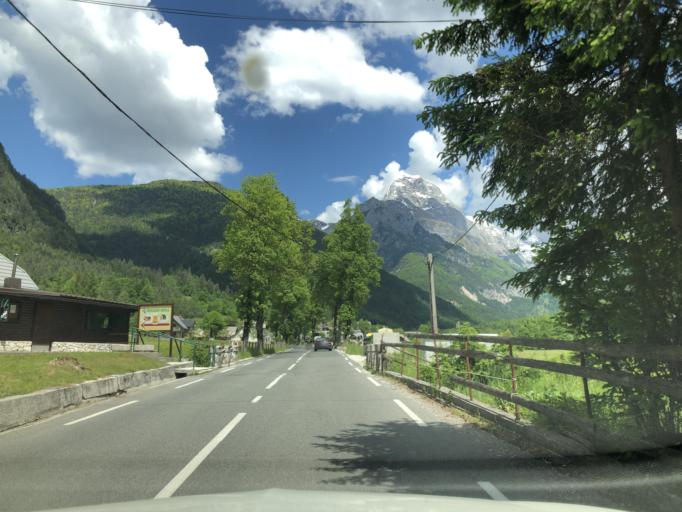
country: SI
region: Bovec
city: Bovec
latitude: 46.4020
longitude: 13.5980
